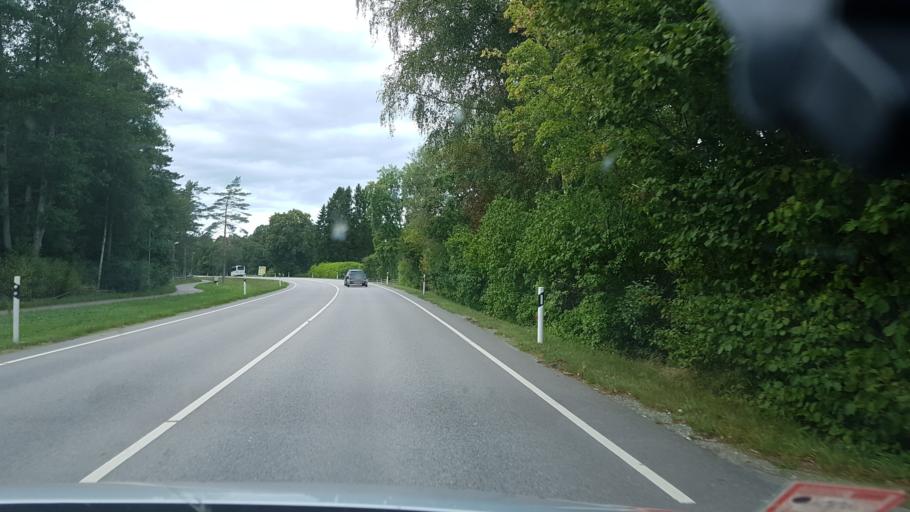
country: EE
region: Saare
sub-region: Kuressaare linn
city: Kuressaare
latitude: 58.2188
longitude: 22.3350
